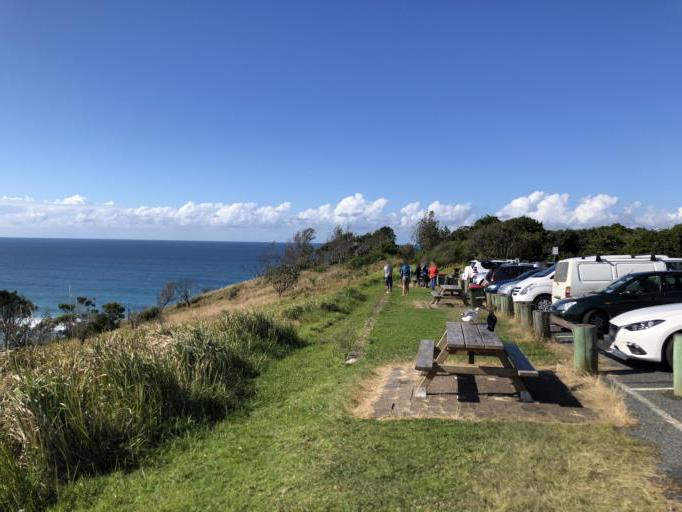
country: AU
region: New South Wales
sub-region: Coffs Harbour
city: Sawtell
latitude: -30.3564
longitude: 153.1052
